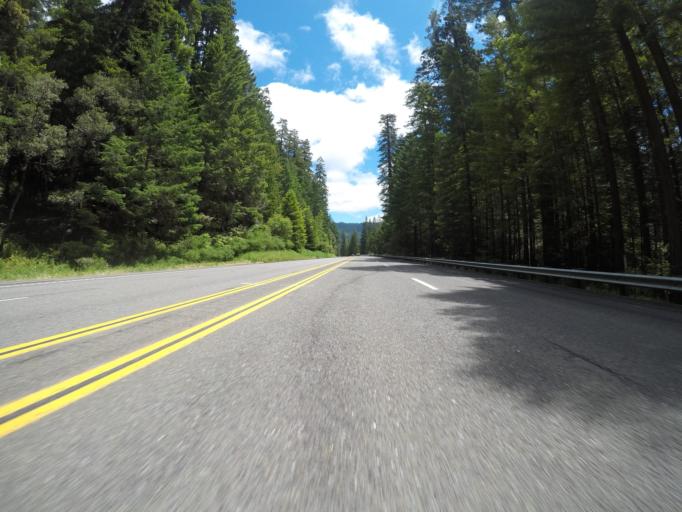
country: US
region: California
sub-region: Humboldt County
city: Redway
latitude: 40.2770
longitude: -123.8840
